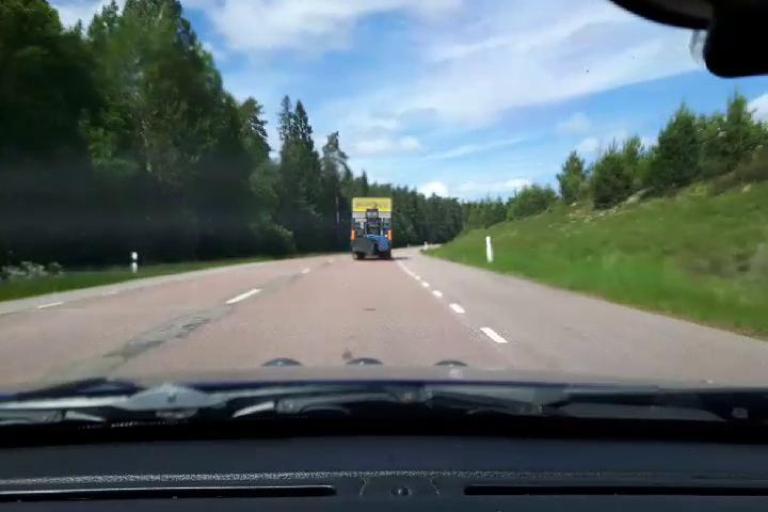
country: SE
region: Uppsala
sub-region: Osthammars Kommun
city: Bjorklinge
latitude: 60.1235
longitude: 17.5095
